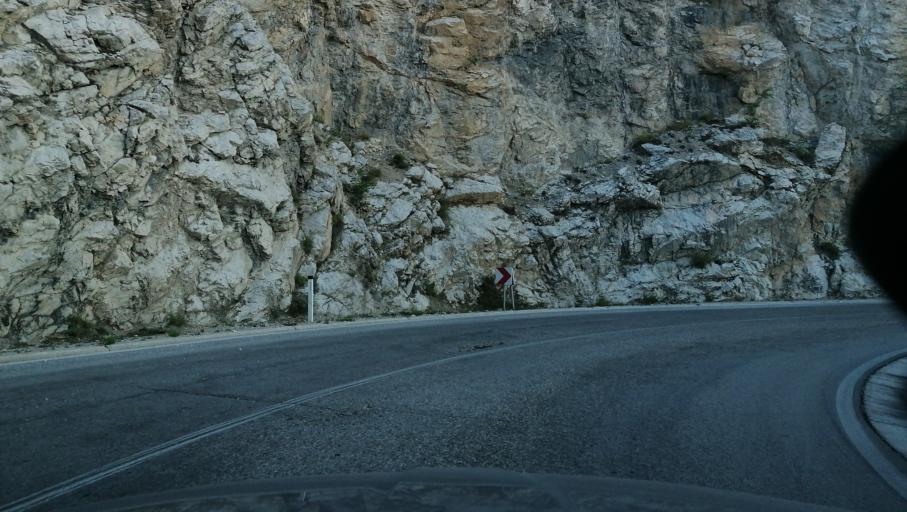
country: BA
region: Federation of Bosnia and Herzegovina
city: Prozor
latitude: 43.8389
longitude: 17.5807
